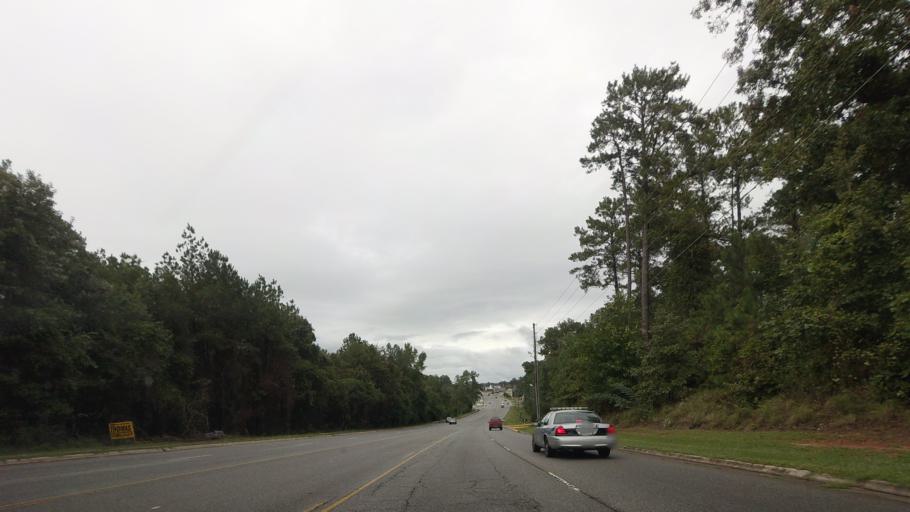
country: US
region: Georgia
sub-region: Houston County
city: Warner Robins
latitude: 32.5816
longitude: -83.6237
